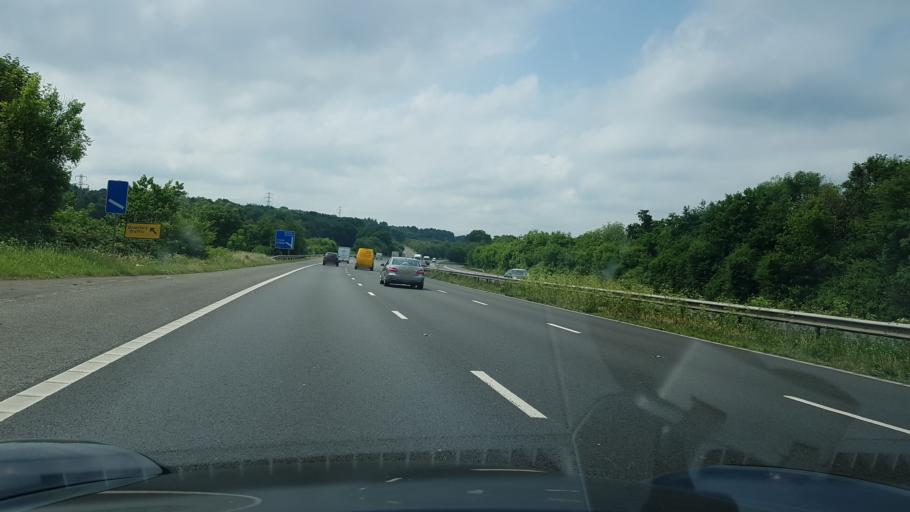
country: GB
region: England
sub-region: West Sussex
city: Maidenbower
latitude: 51.1098
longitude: -0.1389
